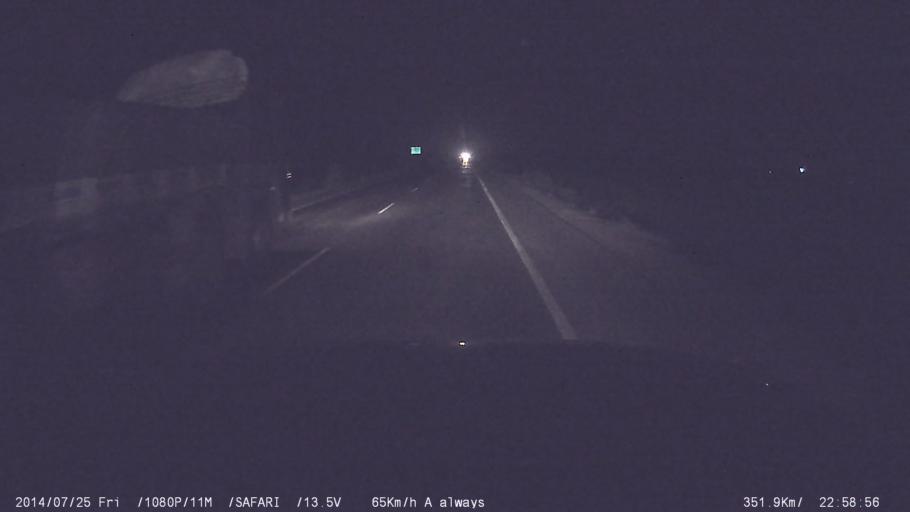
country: IN
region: Tamil Nadu
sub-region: Coimbatore
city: Singanallur
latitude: 10.9628
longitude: 77.0297
